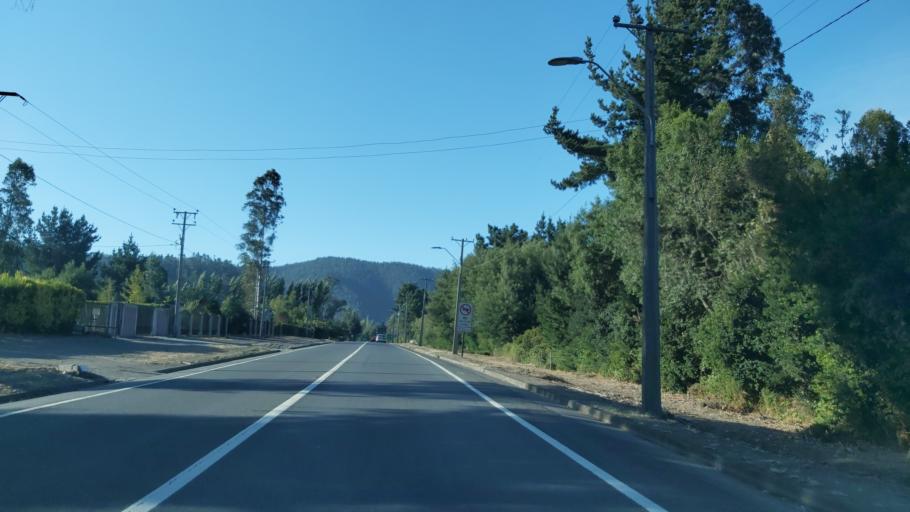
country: CL
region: Biobio
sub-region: Provincia de Concepcion
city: Chiguayante
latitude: -37.0179
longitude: -72.9866
